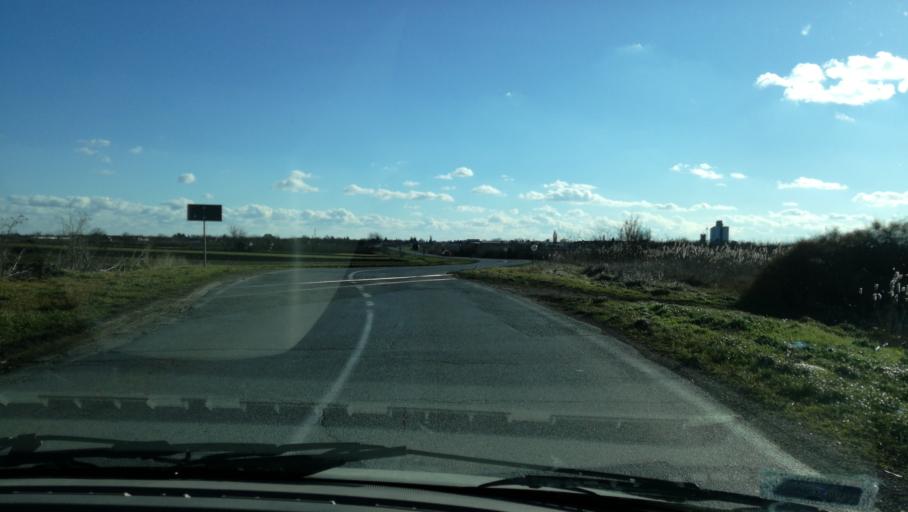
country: RS
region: Autonomna Pokrajina Vojvodina
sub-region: Severnobanatski Okrug
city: Coka
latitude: 45.9550
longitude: 20.1352
